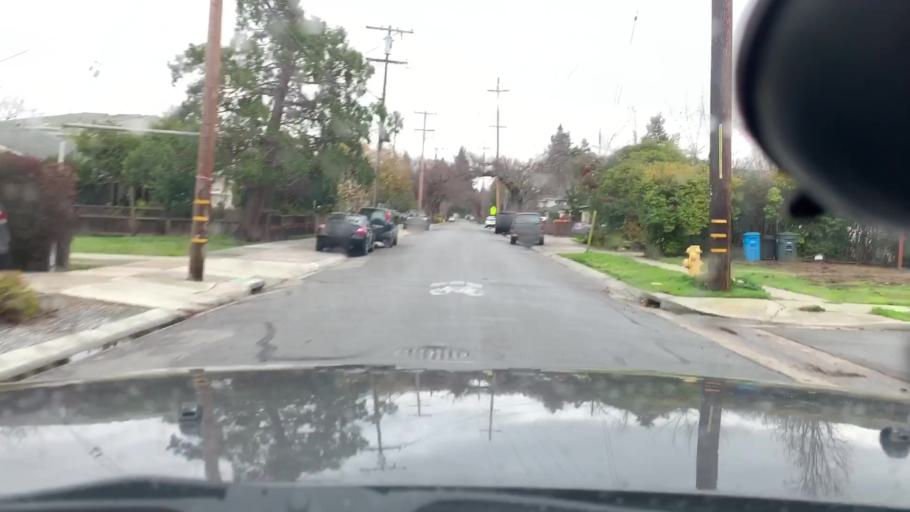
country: US
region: California
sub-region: San Mateo County
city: Atherton
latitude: 37.4580
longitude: -122.2240
